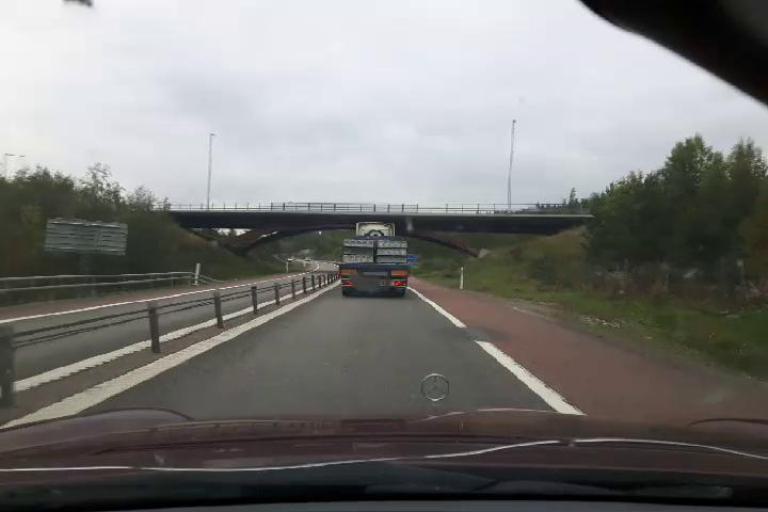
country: SE
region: Vaesternorrland
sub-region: Haernoesands Kommun
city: Haernoesand
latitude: 62.7824
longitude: 17.9186
